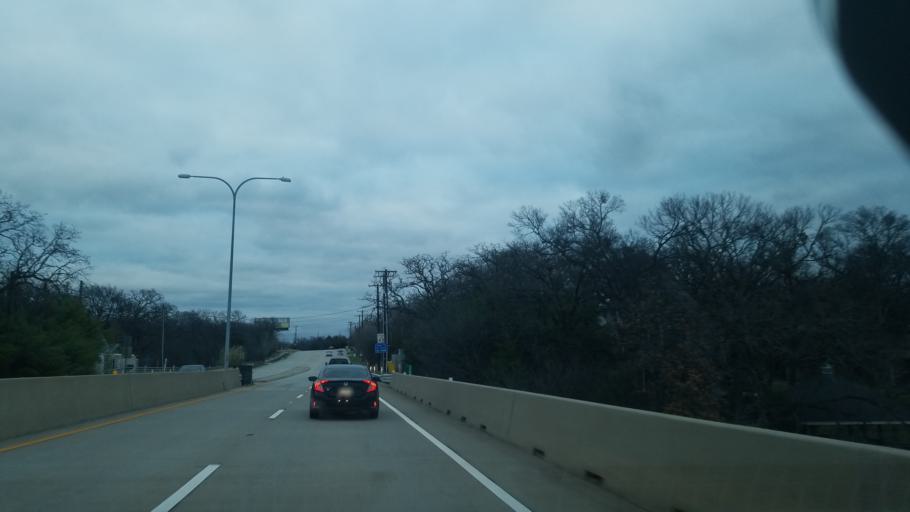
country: US
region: Texas
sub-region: Denton County
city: Lake Dallas
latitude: 33.1404
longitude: -96.9901
